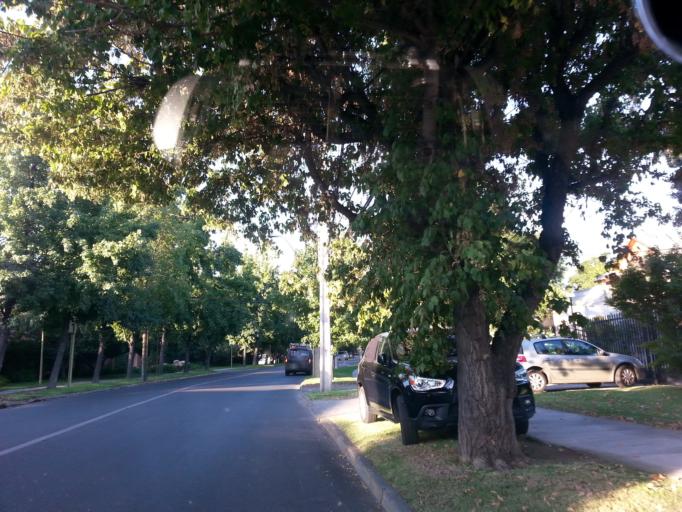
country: CL
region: Santiago Metropolitan
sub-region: Provincia de Santiago
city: Villa Presidente Frei, Nunoa, Santiago, Chile
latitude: -33.3901
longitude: -70.5354
